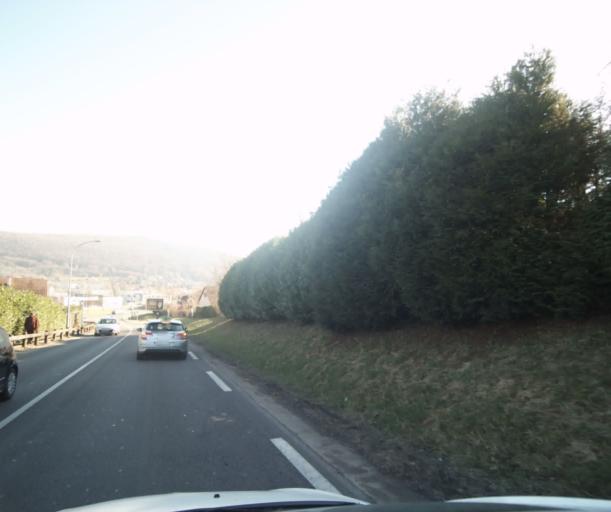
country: FR
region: Franche-Comte
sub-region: Departement du Doubs
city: Avanne-Aveney
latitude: 47.2159
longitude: 5.9598
